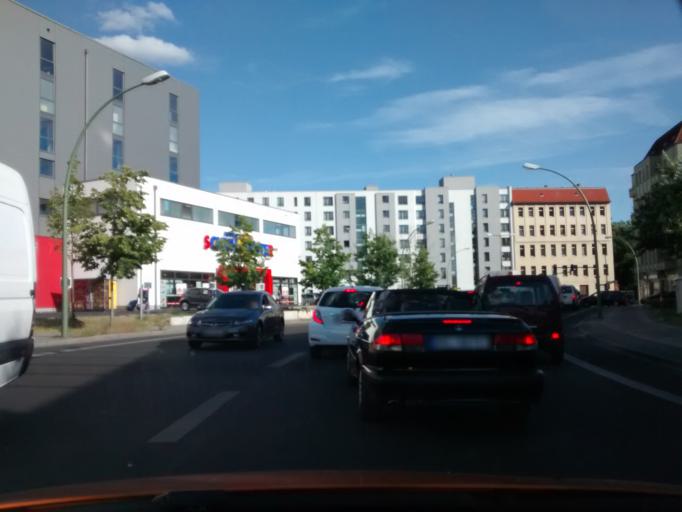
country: DE
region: Berlin
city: Wedding Bezirk
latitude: 52.5365
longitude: 13.3561
